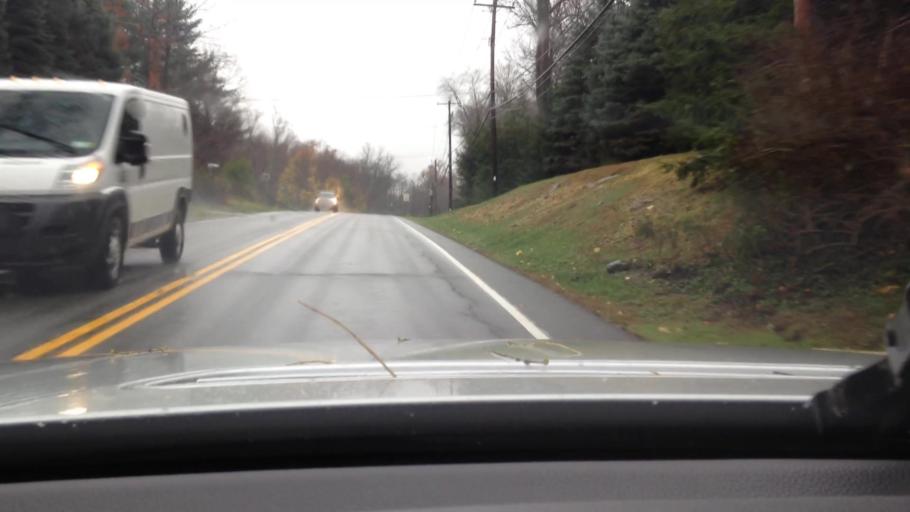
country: US
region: New York
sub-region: Orange County
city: West Point
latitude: 41.3885
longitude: -73.9348
